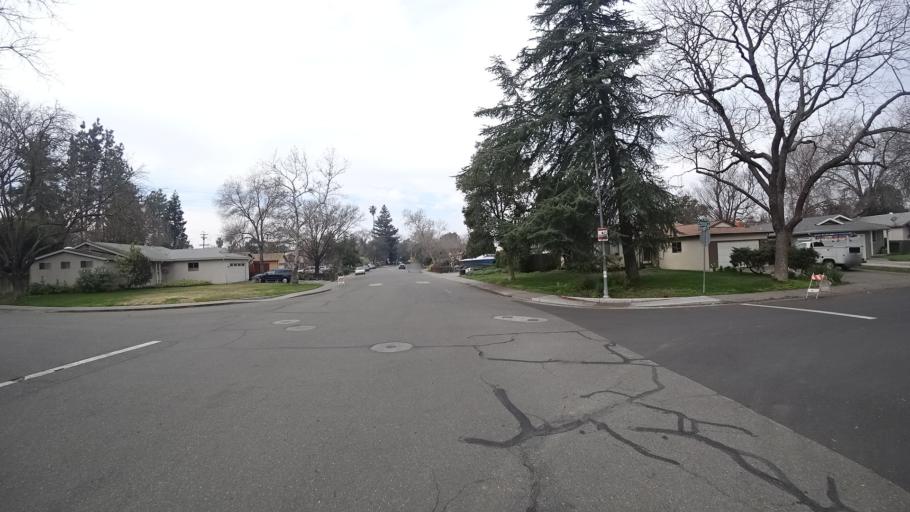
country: US
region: California
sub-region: Yolo County
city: Davis
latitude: 38.5575
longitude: -121.7316
